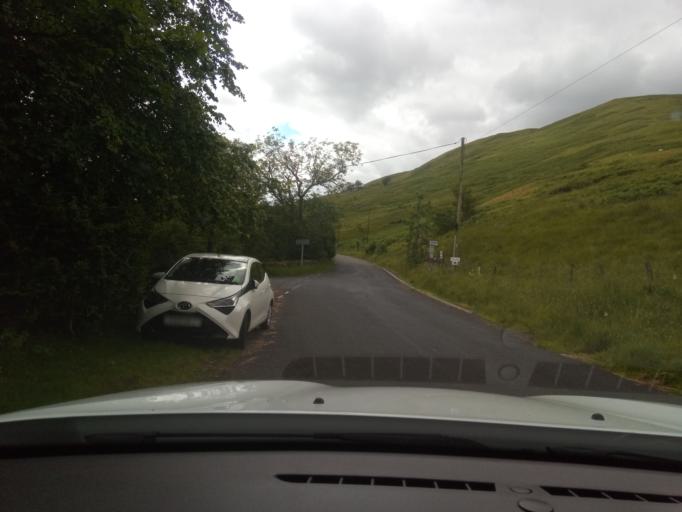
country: GB
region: Scotland
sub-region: The Scottish Borders
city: Innerleithen
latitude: 55.4478
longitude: -3.1037
